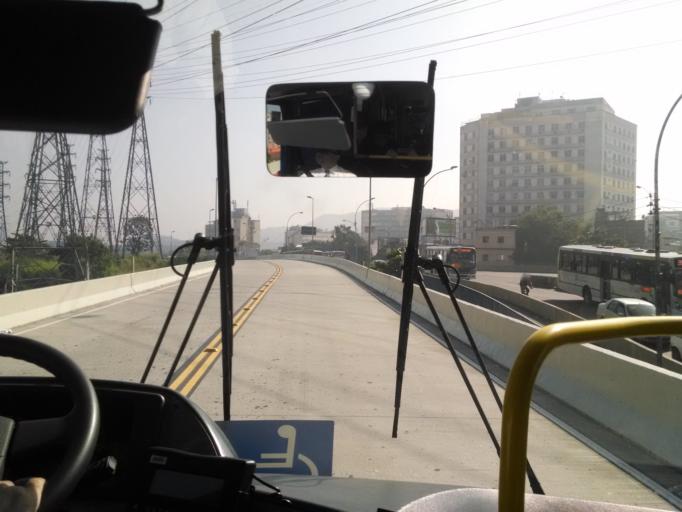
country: BR
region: Rio de Janeiro
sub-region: Sao Joao De Meriti
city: Sao Joao de Meriti
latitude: -22.8749
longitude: -43.3352
